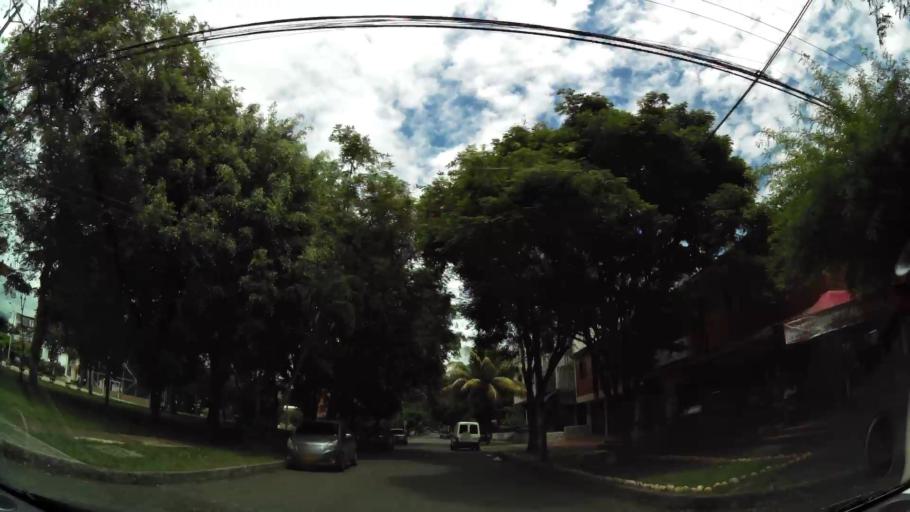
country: CO
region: Valle del Cauca
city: Cali
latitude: 3.3830
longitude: -76.5304
